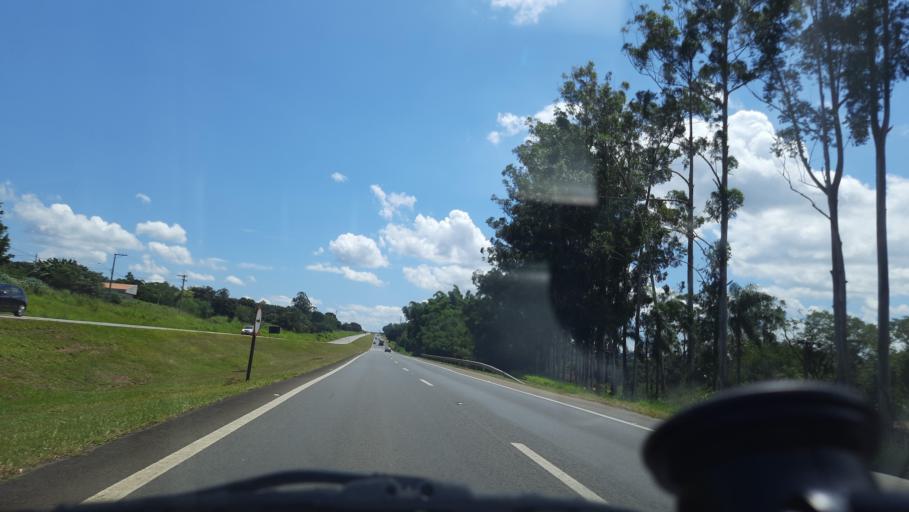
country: BR
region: Sao Paulo
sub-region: Moji-Guacu
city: Mogi-Gaucu
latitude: -22.2429
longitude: -46.9780
